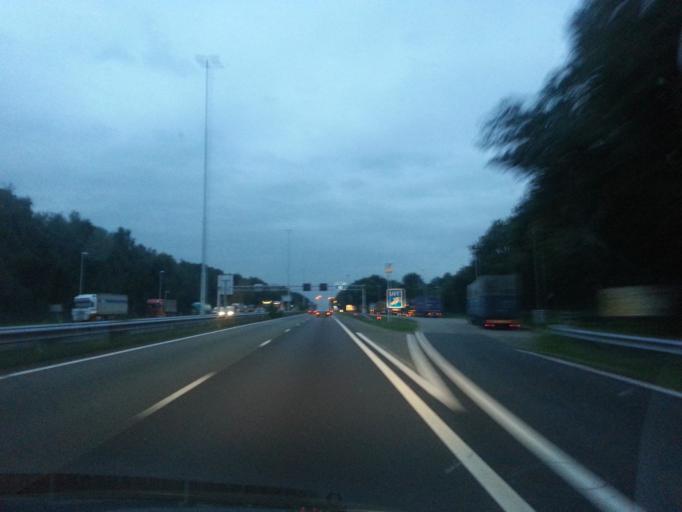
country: NL
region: North Brabant
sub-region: Gemeente Oisterwijk
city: Oisterwijk
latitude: 51.5462
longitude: 5.1491
